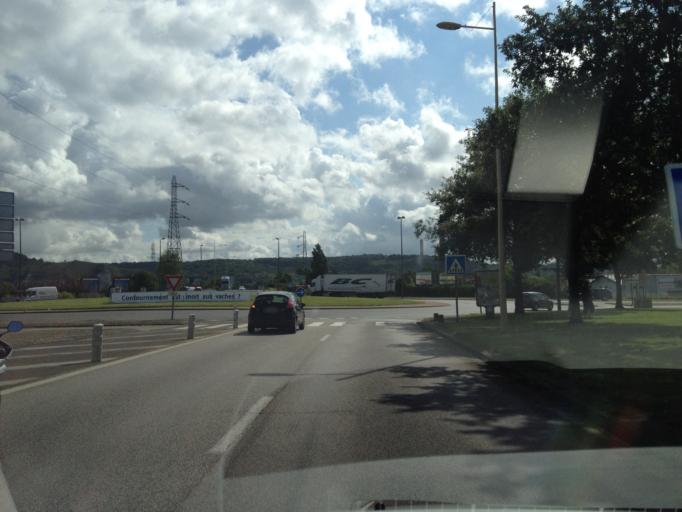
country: FR
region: Haute-Normandie
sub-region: Departement de la Seine-Maritime
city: Saint-Etienne-du-Rouvray
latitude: 49.3676
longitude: 1.1053
